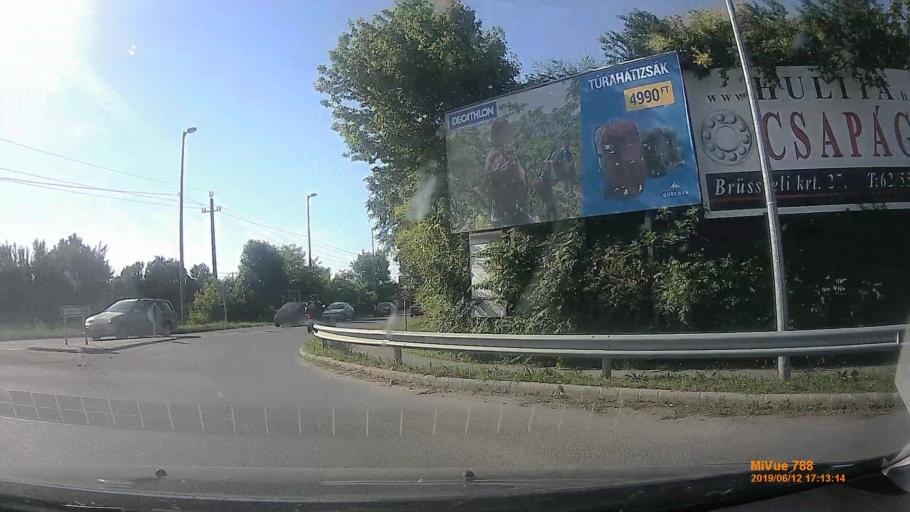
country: HU
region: Csongrad
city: Szeged
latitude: 46.2321
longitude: 20.1742
